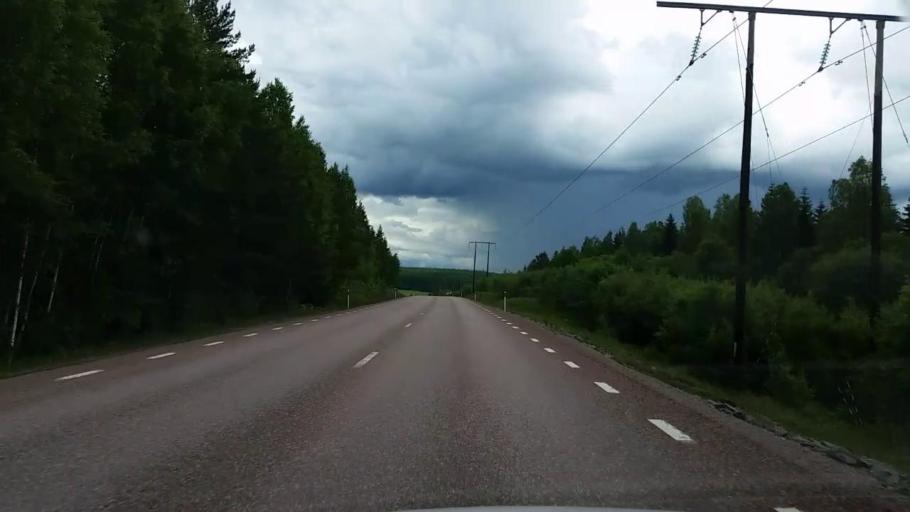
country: SE
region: Gaevleborg
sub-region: Hofors Kommun
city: Hofors
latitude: 60.5312
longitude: 16.4567
